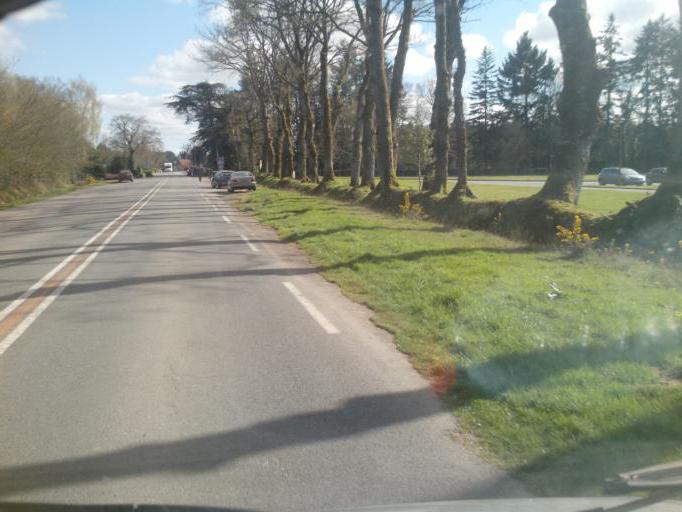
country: FR
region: Brittany
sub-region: Departement d'Ille-et-Vilaine
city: Paimpont
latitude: 48.0250
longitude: -2.1730
